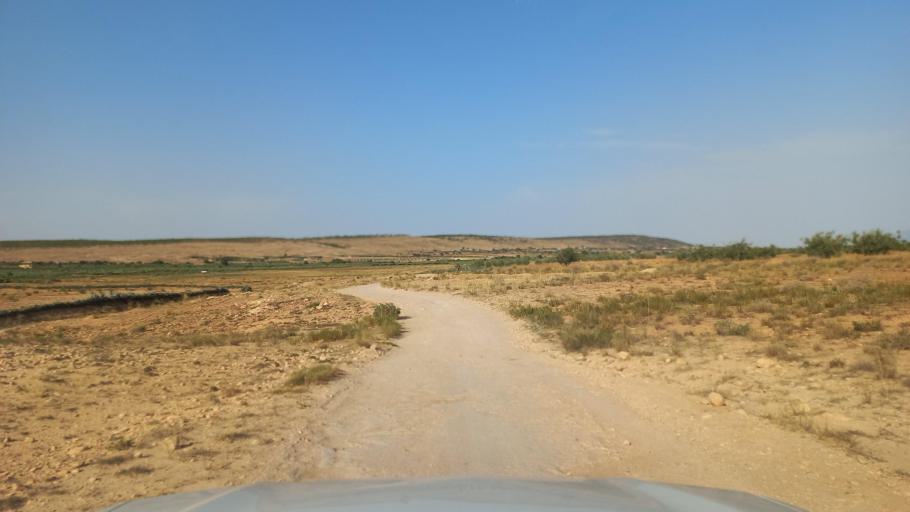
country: TN
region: Al Qasrayn
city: Kasserine
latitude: 35.3550
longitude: 8.8500
